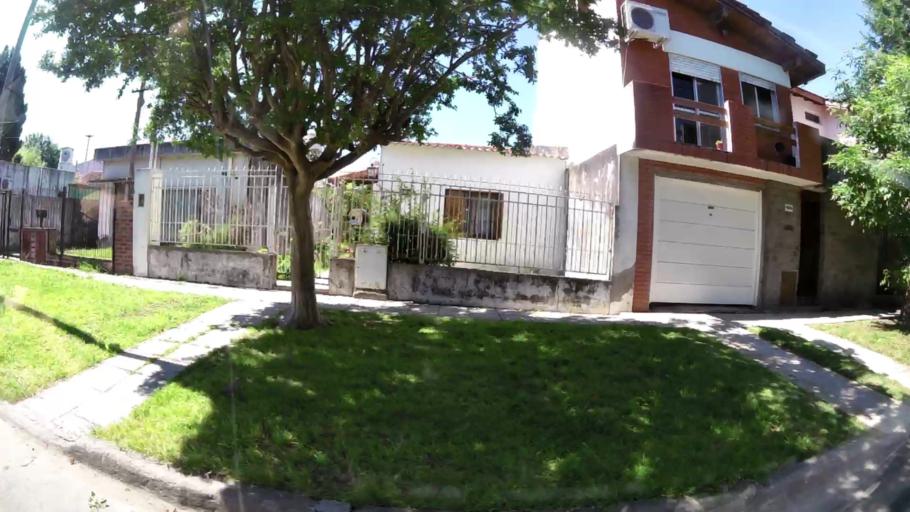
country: AR
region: Buenos Aires
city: Ituzaingo
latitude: -34.6636
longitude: -58.6685
